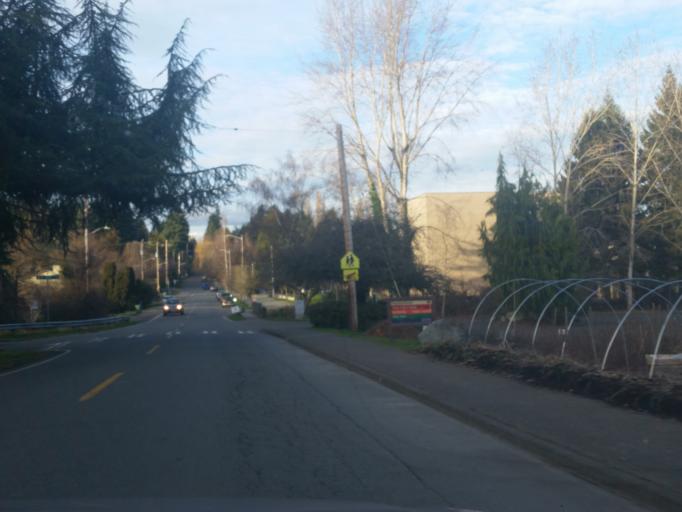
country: US
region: Washington
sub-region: King County
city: Lake Forest Park
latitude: 47.7063
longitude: -122.2962
